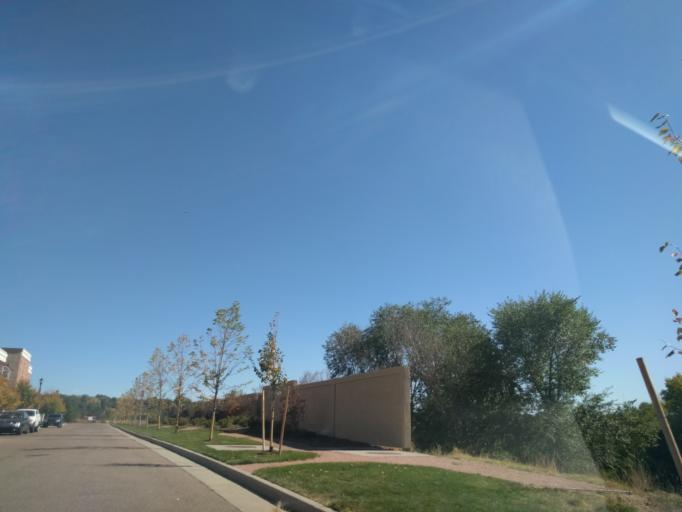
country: US
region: Colorado
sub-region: El Paso County
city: Colorado Springs
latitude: 38.8204
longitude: -104.8218
